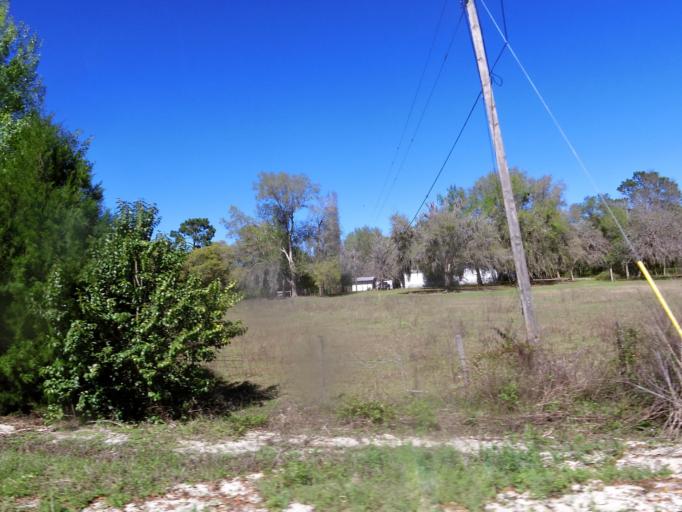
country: US
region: Florida
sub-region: Clay County
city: Keystone Heights
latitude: 29.8115
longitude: -82.0451
